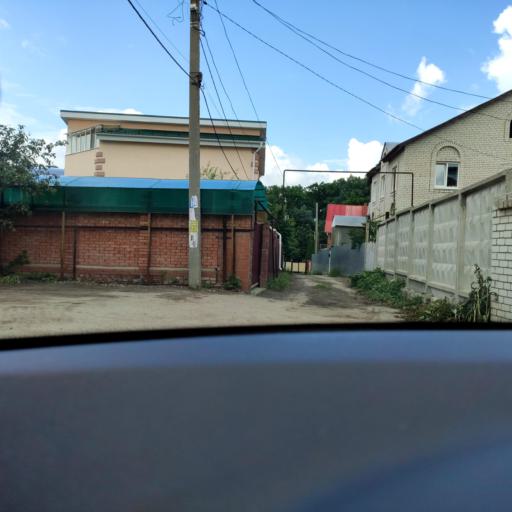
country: RU
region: Samara
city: Samara
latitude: 53.2661
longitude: 50.1975
